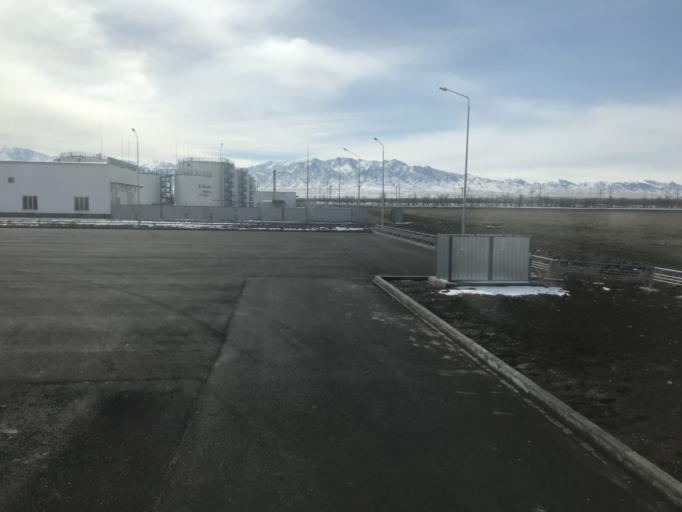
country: KZ
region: Zhambyl
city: Sarykemer
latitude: 43.0082
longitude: 71.7846
